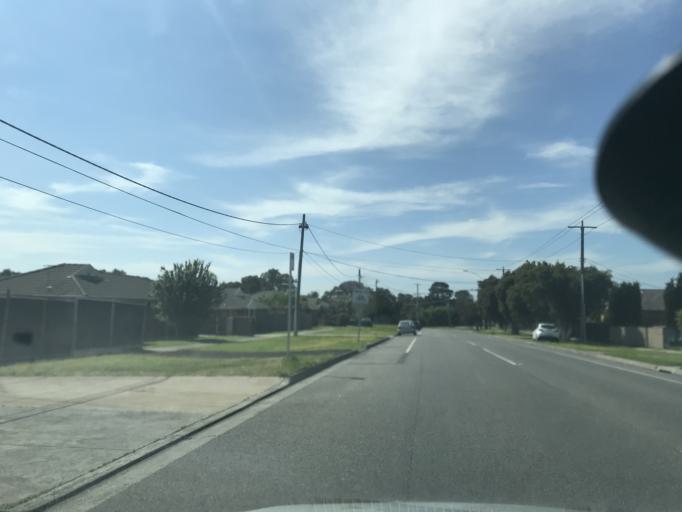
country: AU
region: Victoria
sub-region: Whittlesea
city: Epping
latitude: -37.6490
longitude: 145.0305
